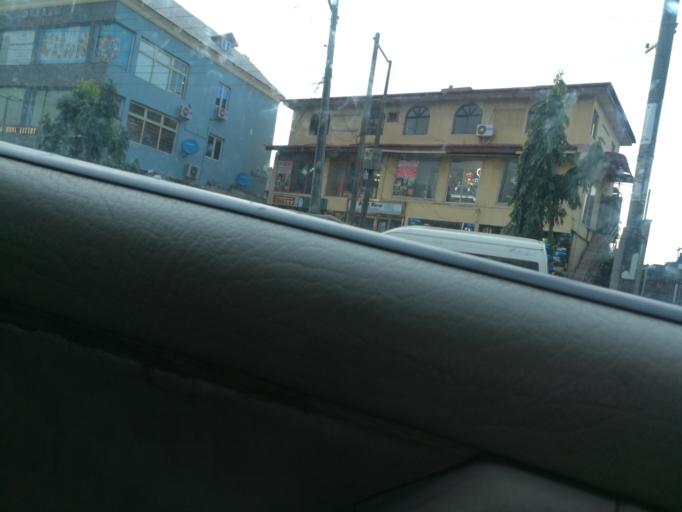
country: NG
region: Lagos
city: Ikeja
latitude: 6.6048
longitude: 3.3467
